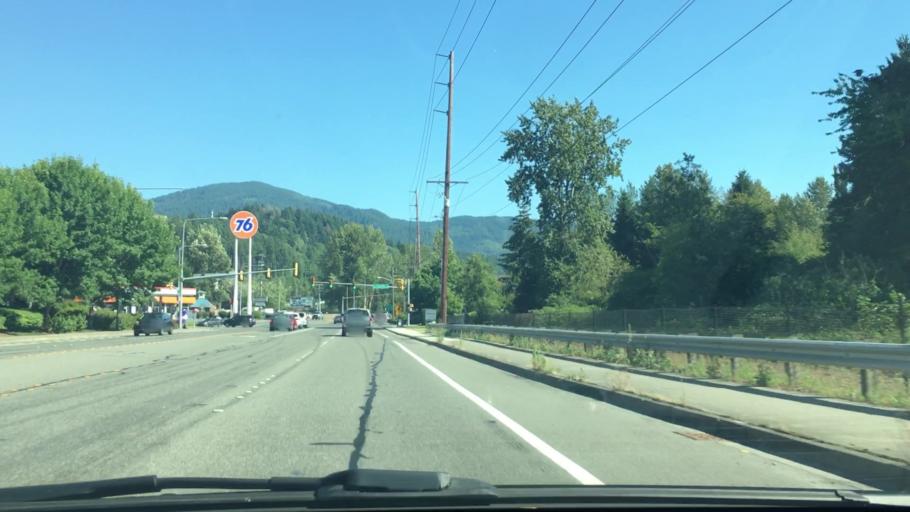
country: US
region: Washington
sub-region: King County
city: Issaquah
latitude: 47.5452
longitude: -122.0383
